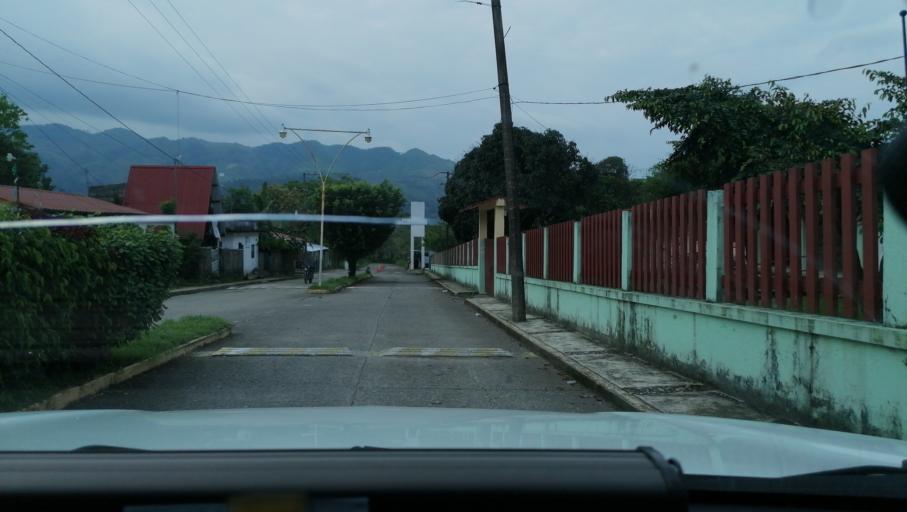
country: MX
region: Chiapas
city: Ixtacomitan
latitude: 17.3434
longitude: -93.1309
